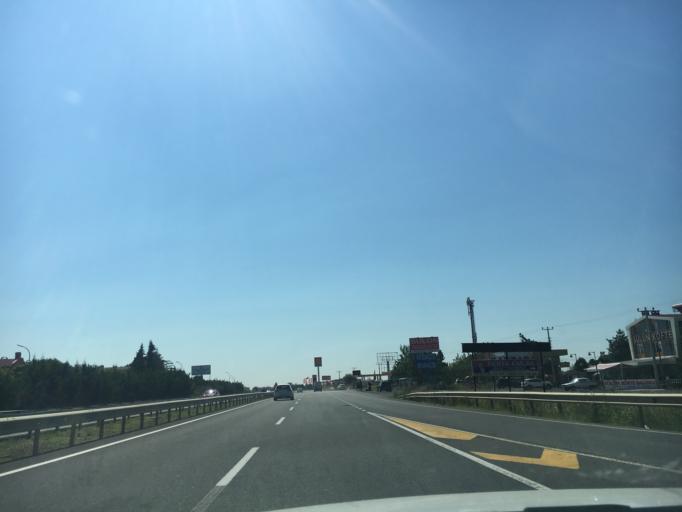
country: TR
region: Tekirdag
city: Marmara Ereglisi
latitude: 40.9731
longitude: 27.8796
